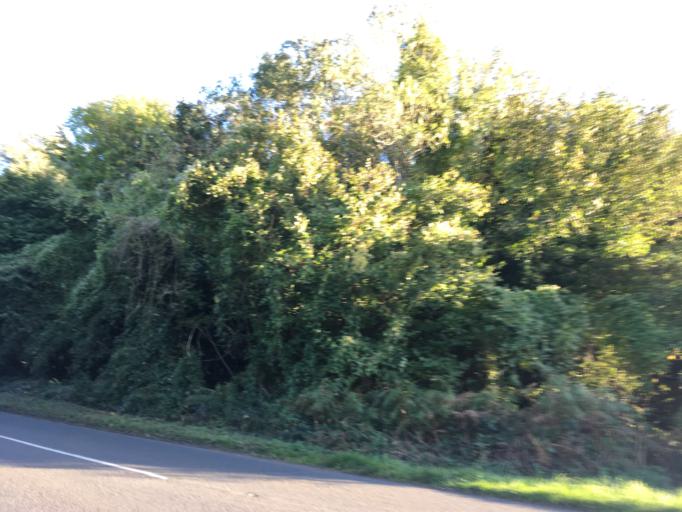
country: GB
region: England
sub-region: South Gloucestershire
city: Alveston
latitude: 51.5950
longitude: -2.5647
